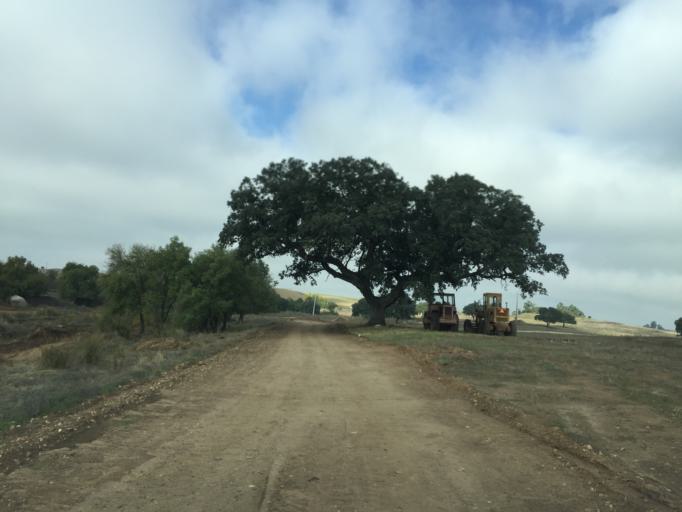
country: PT
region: Portalegre
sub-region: Fronteira
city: Fronteira
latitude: 39.0694
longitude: -7.6183
